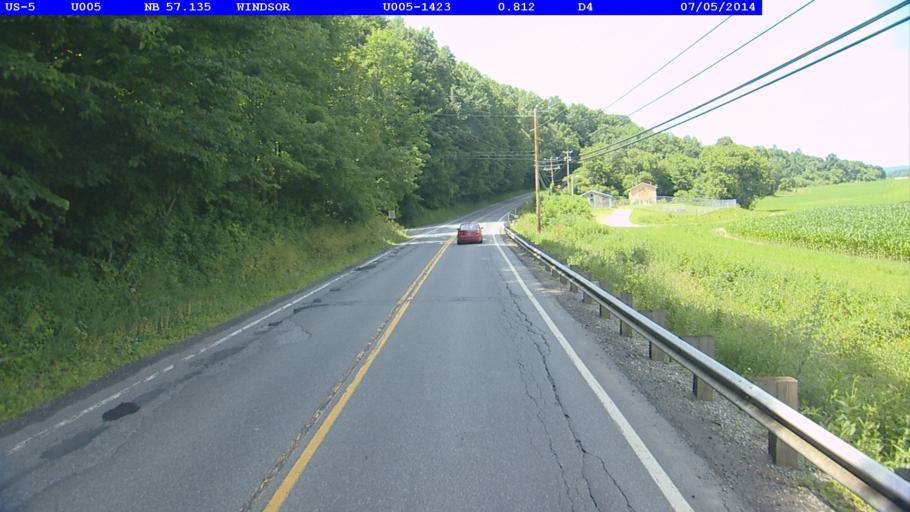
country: US
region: Vermont
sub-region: Windsor County
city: Windsor
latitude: 43.4403
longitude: -72.3981
